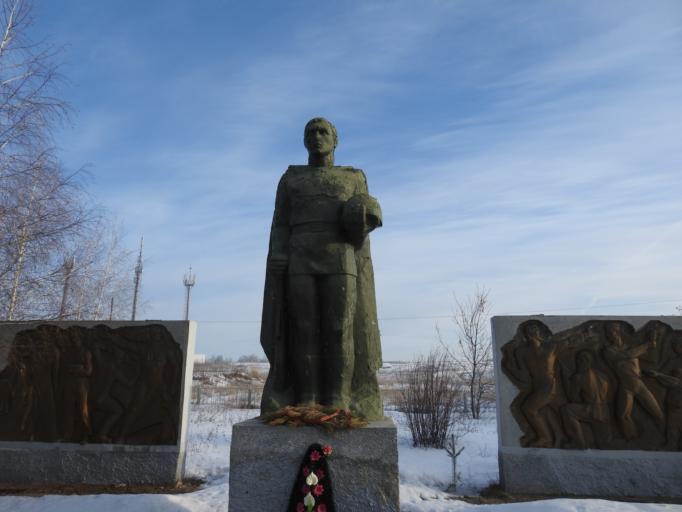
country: RU
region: Saratov
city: Krasnyy Oktyabr'
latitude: 51.4971
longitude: 45.7167
